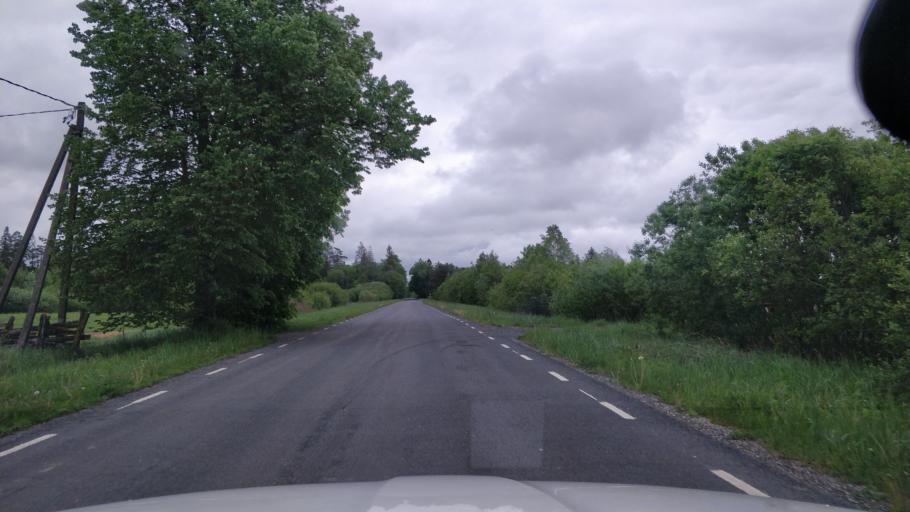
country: EE
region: Raplamaa
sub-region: Maerjamaa vald
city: Marjamaa
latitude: 58.7598
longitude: 24.2516
